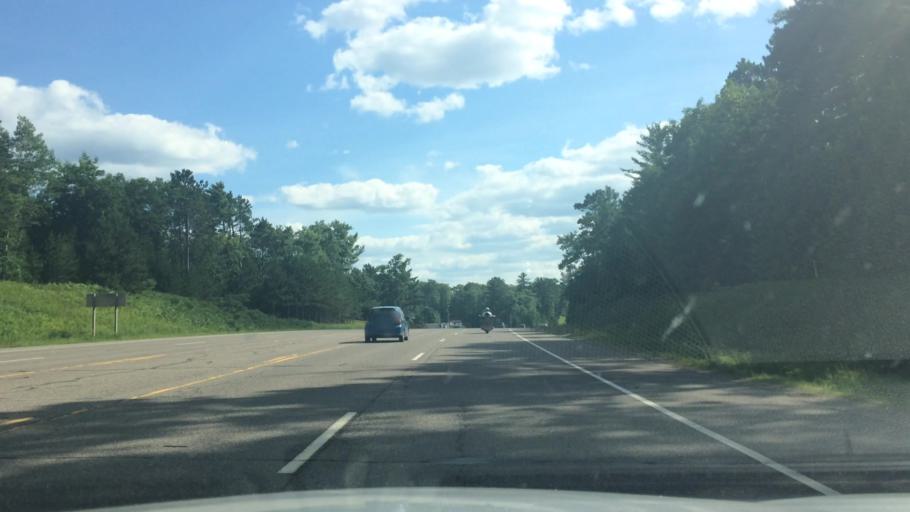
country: US
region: Wisconsin
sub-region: Vilas County
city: Lac du Flambeau
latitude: 45.8409
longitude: -89.7075
